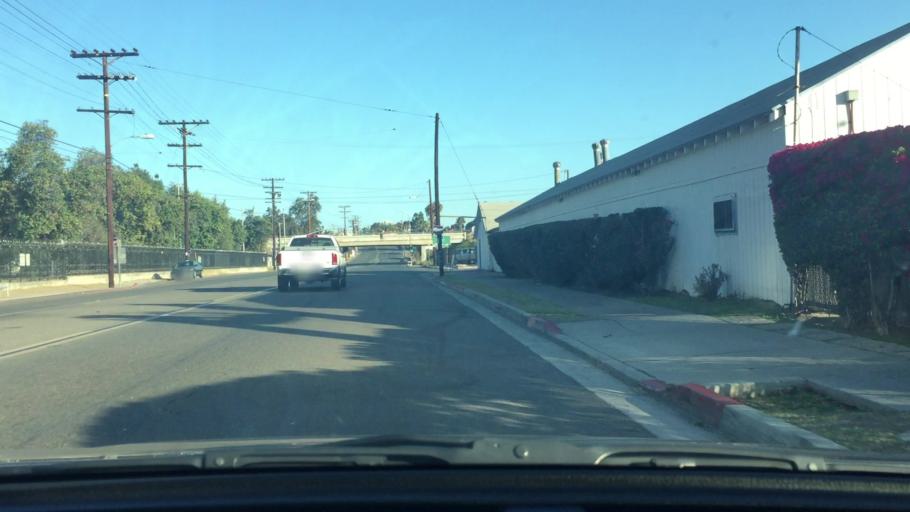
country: US
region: California
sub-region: San Diego County
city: National City
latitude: 32.6897
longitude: -117.1214
